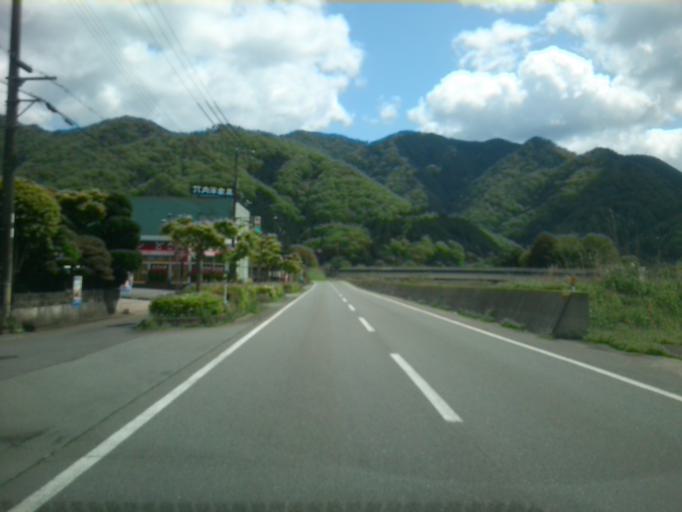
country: JP
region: Hyogo
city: Toyooka
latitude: 35.4495
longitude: 134.8723
